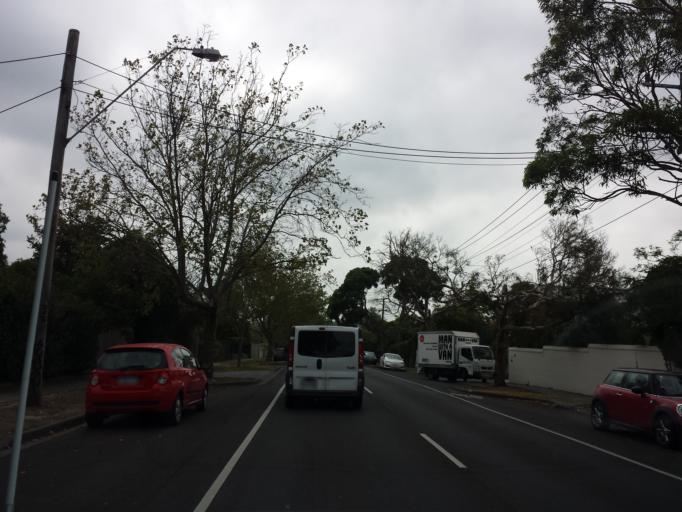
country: AU
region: Victoria
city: Glenferrie
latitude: -37.8334
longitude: 145.0430
